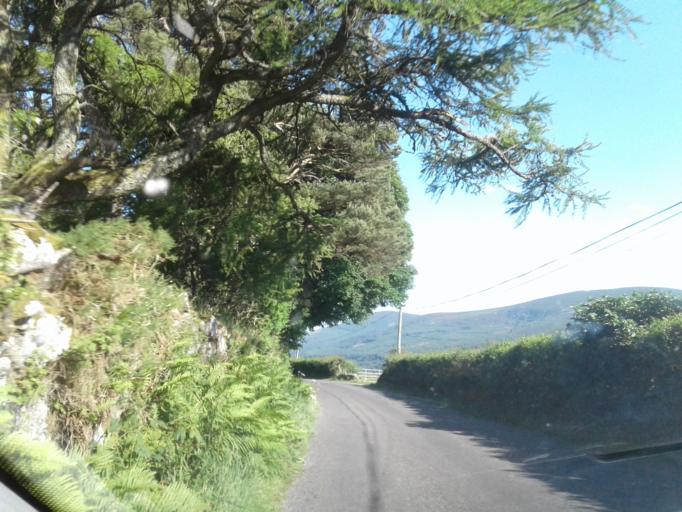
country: IE
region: Leinster
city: Ballinteer
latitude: 53.1980
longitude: -6.2869
